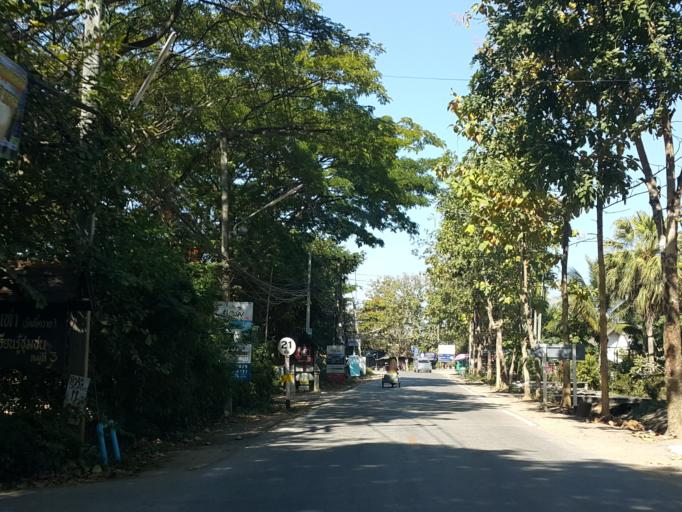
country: TH
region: Chiang Mai
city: San Sai
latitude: 18.8522
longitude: 98.9865
